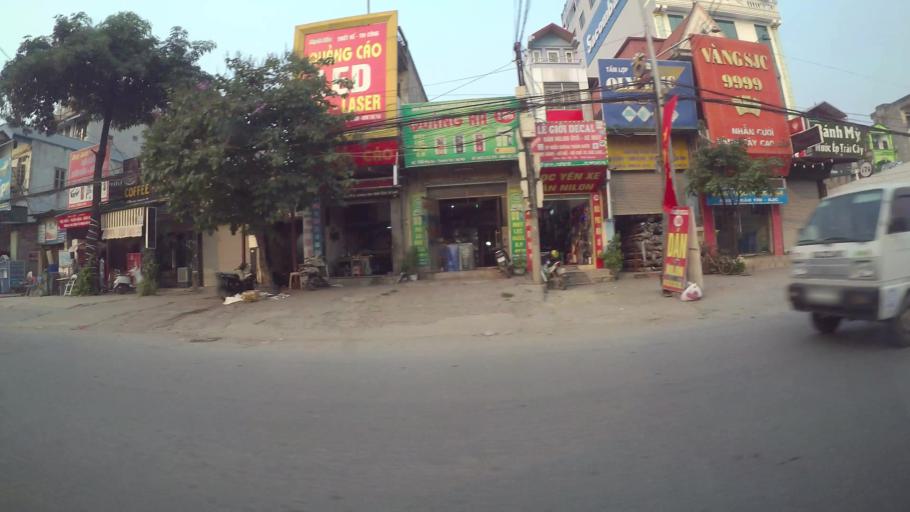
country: VN
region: Ha Noi
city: Thuong Tin
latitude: 20.8723
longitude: 105.8643
